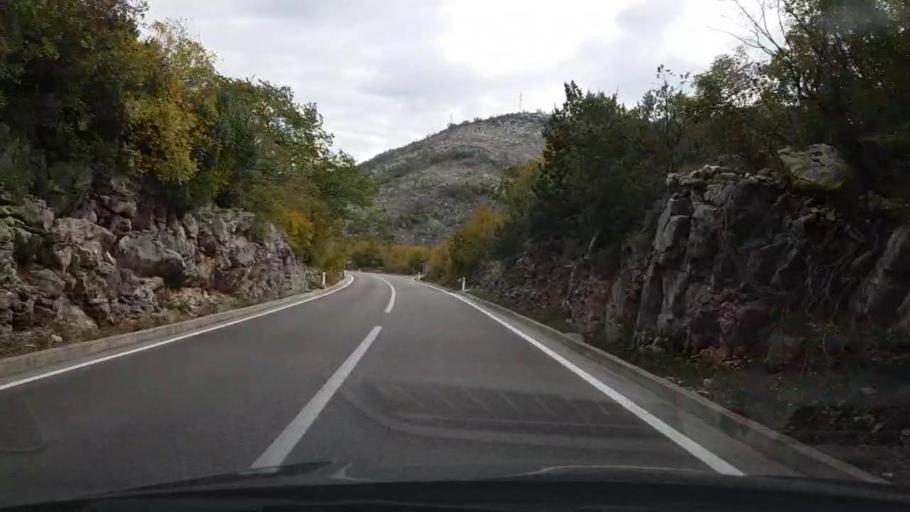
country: BA
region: Republika Srpska
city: Trebinje
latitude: 42.6848
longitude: 18.2885
